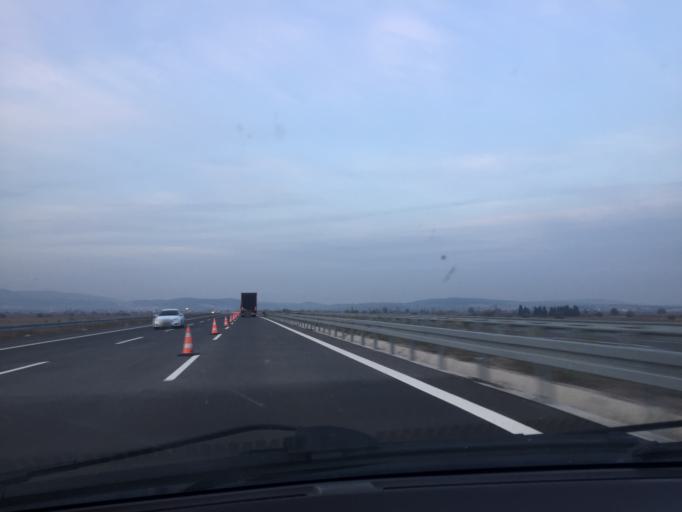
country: TR
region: Manisa
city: Halitpasa
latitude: 38.7385
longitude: 27.6577
